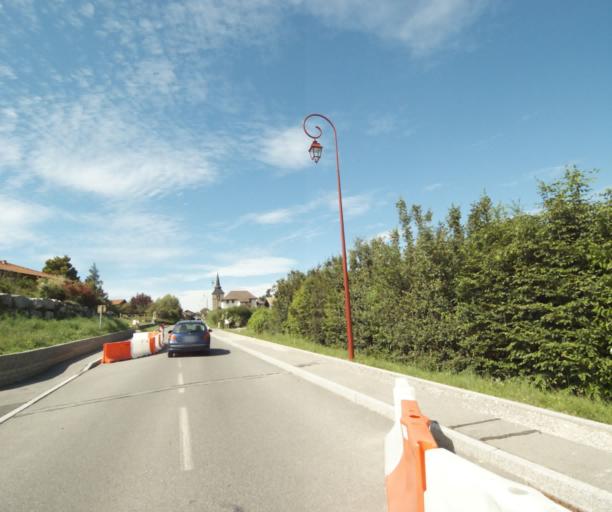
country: FR
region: Rhone-Alpes
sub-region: Departement de la Haute-Savoie
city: Perrignier
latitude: 46.3013
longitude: 6.4573
